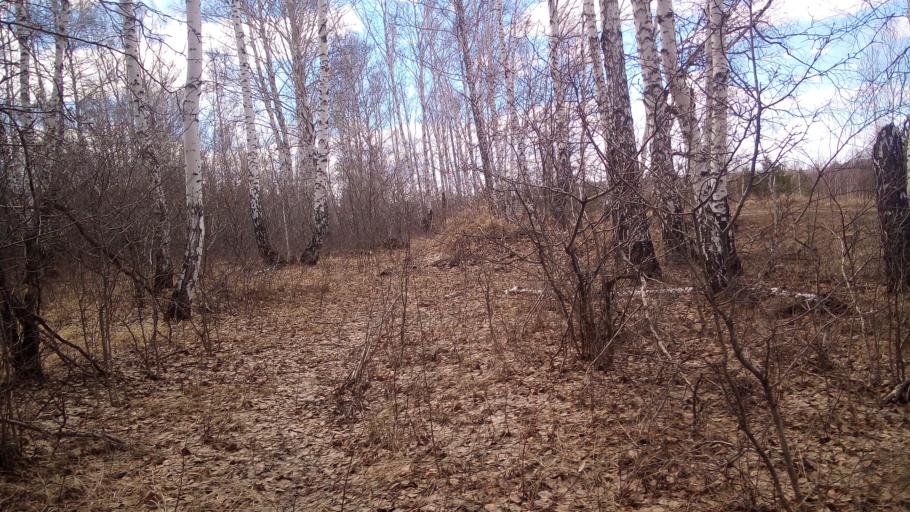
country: RU
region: Chelyabinsk
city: Sargazy
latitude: 55.1223
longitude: 61.2501
